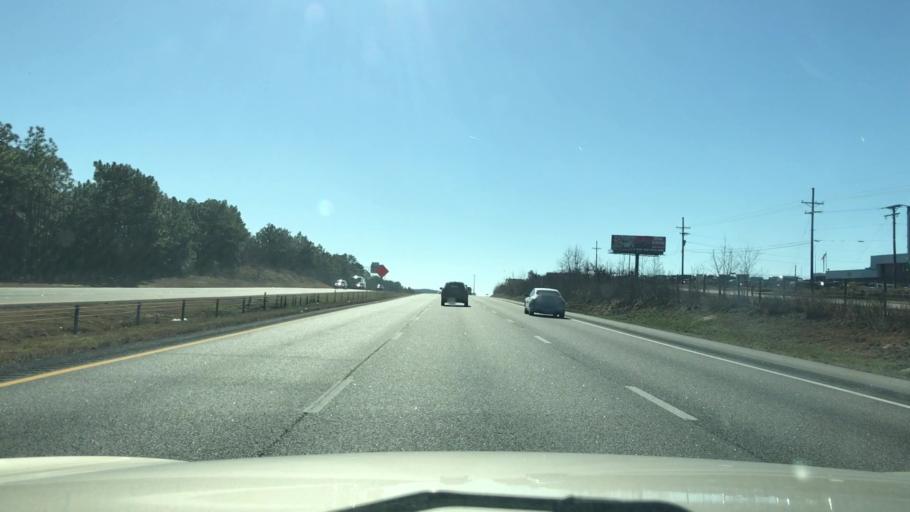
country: US
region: South Carolina
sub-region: Lexington County
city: Pineridge
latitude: 33.8679
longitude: -81.0335
